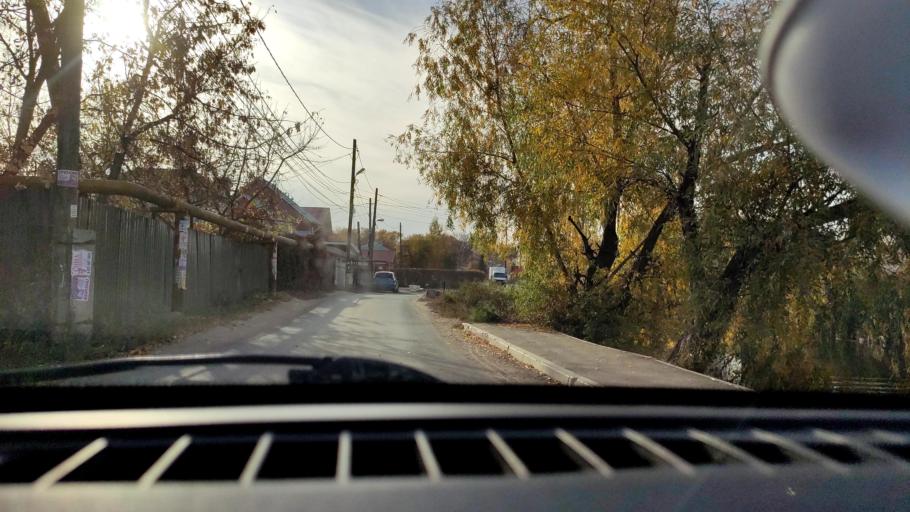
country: RU
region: Samara
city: Petra-Dubrava
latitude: 53.2934
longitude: 50.2797
